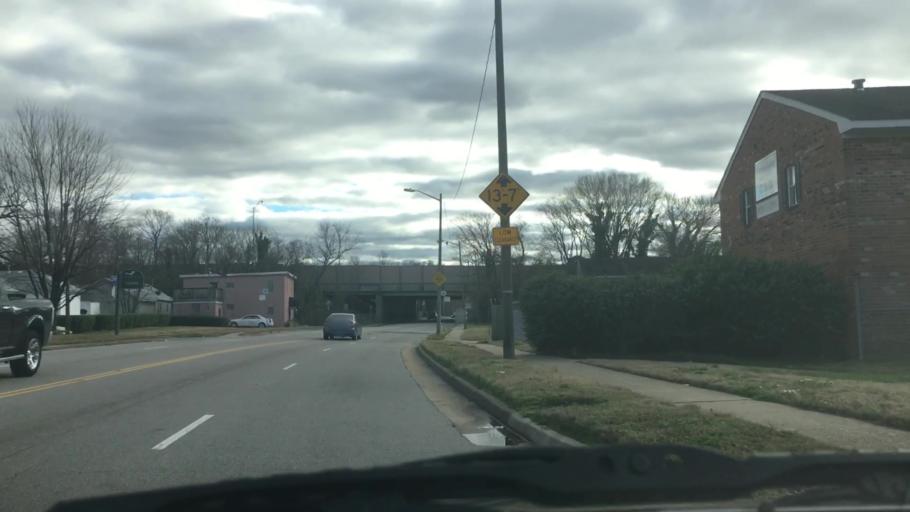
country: US
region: Virginia
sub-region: City of Norfolk
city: Norfolk
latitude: 36.9048
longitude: -76.2431
